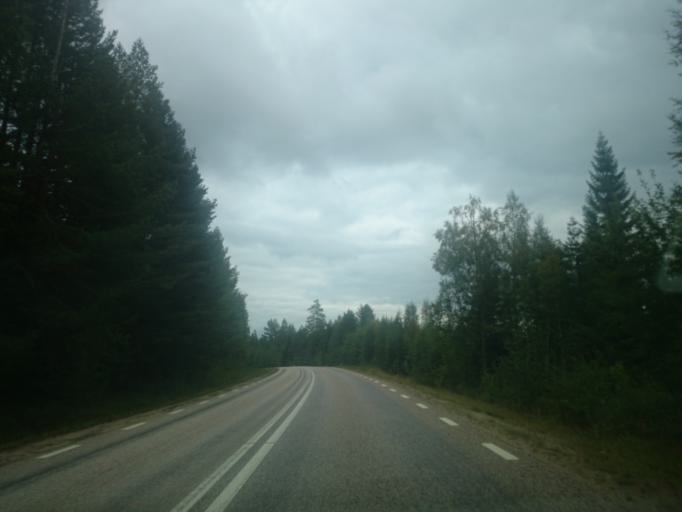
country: SE
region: Gaevleborg
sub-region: Ljusdals Kommun
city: Farila
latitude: 61.9788
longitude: 15.1206
